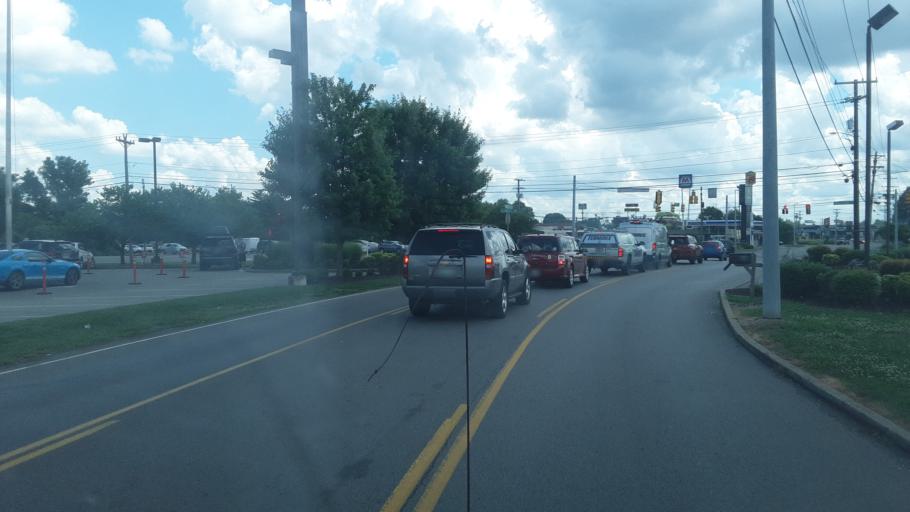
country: US
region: Tennessee
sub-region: Montgomery County
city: Clarksville
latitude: 36.5976
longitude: -87.2864
